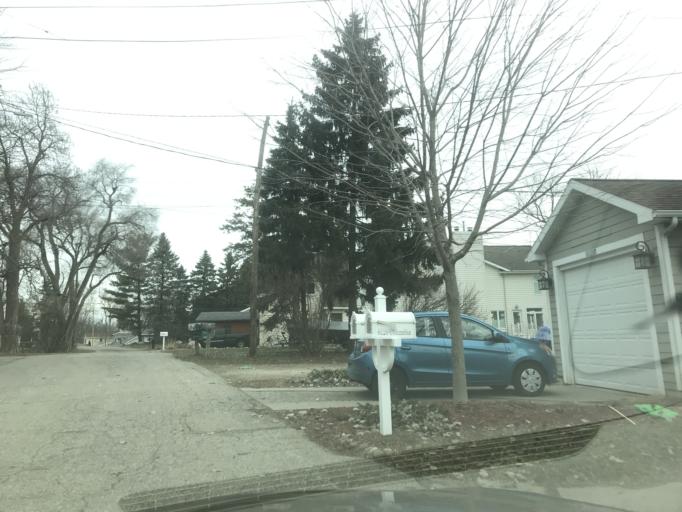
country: US
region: Michigan
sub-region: Ingham County
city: Haslett
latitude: 42.7599
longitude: -84.4086
